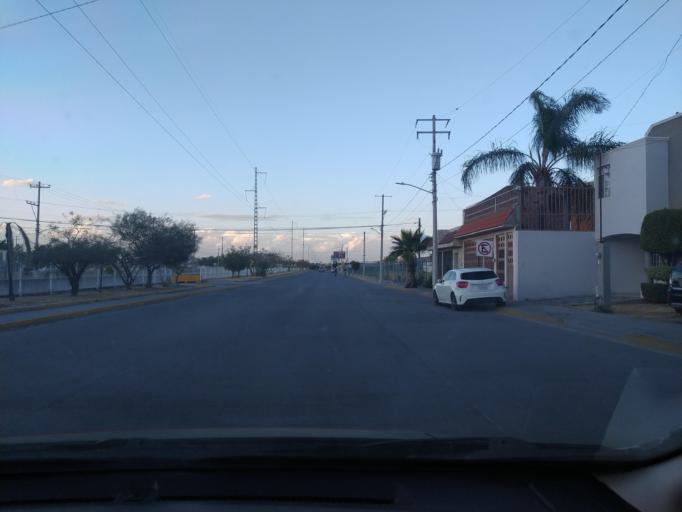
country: LA
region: Oudomxai
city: Muang La
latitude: 21.0176
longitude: 101.8696
